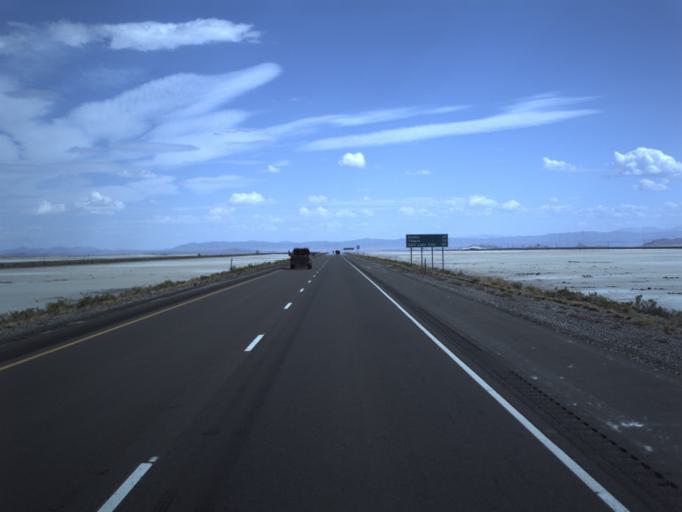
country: US
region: Utah
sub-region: Tooele County
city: Wendover
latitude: 40.7300
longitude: -113.4597
